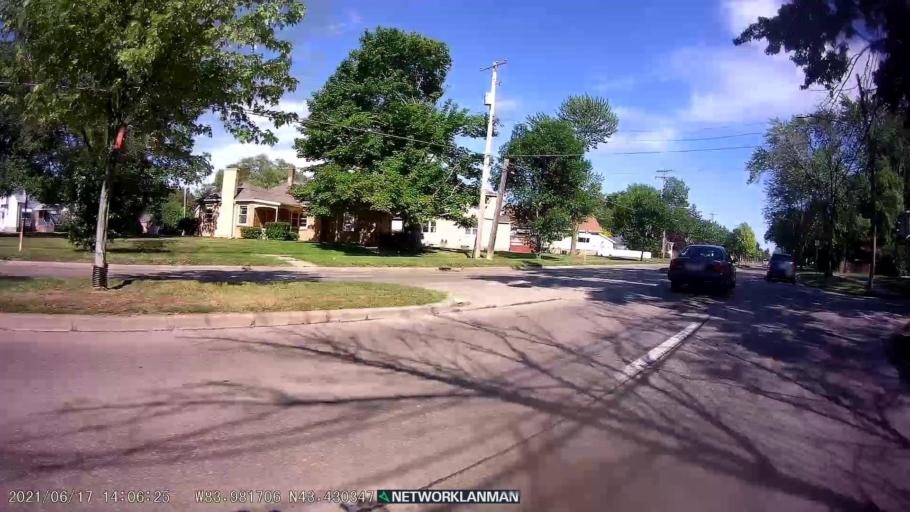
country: US
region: Michigan
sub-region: Saginaw County
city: Saginaw
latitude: 43.4302
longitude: -83.9814
